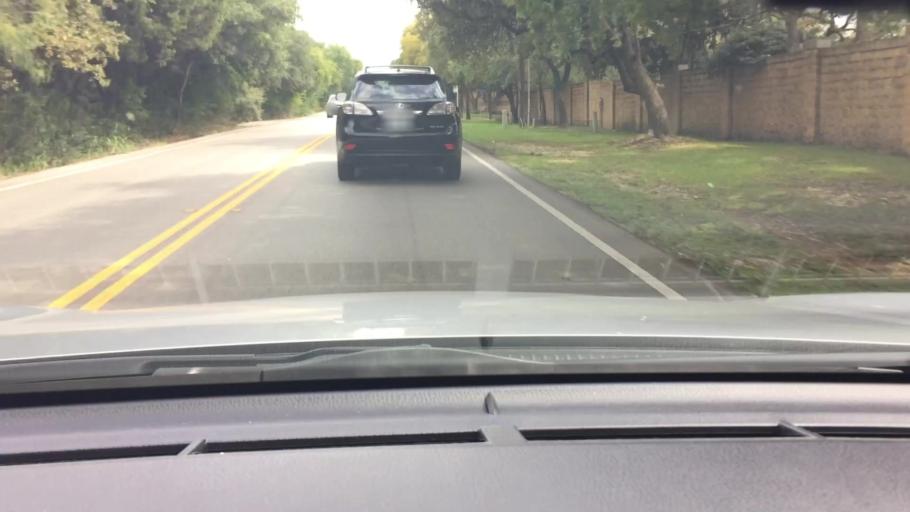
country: US
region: Texas
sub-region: Bexar County
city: Castle Hills
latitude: 29.5463
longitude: -98.5348
